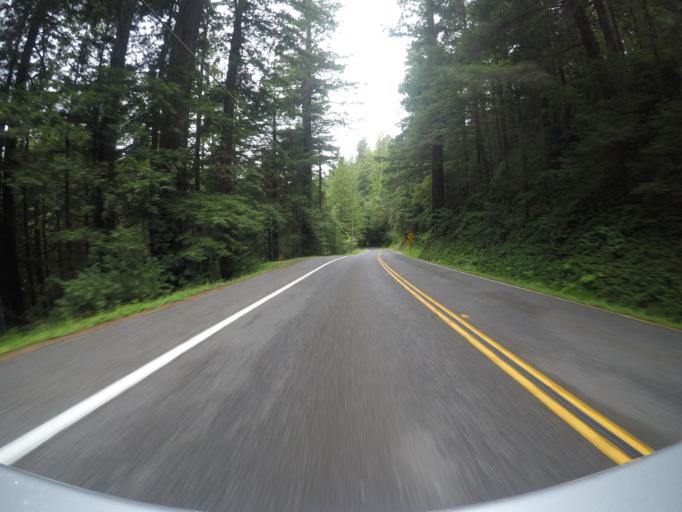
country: US
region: California
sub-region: Humboldt County
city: Rio Dell
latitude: 40.4057
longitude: -123.9518
